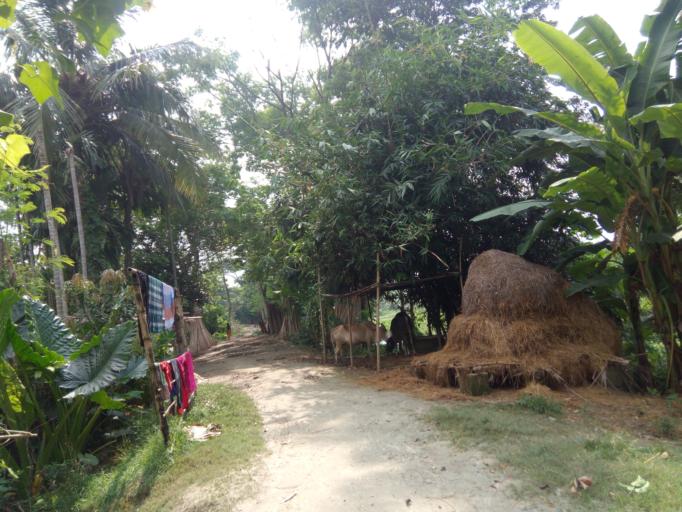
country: BD
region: Khulna
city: Kalia
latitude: 23.0594
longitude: 89.6542
